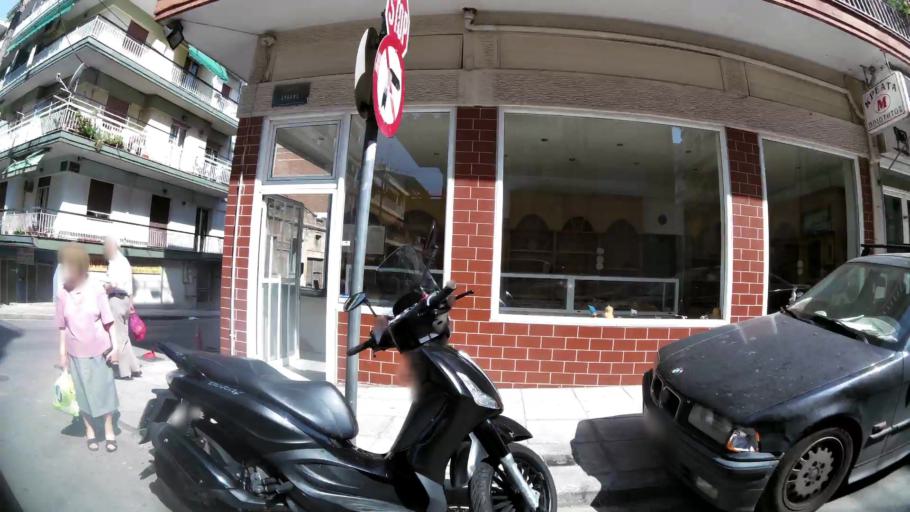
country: GR
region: Central Macedonia
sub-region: Nomos Thessalonikis
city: Thessaloniki
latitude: 40.6472
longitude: 22.9373
